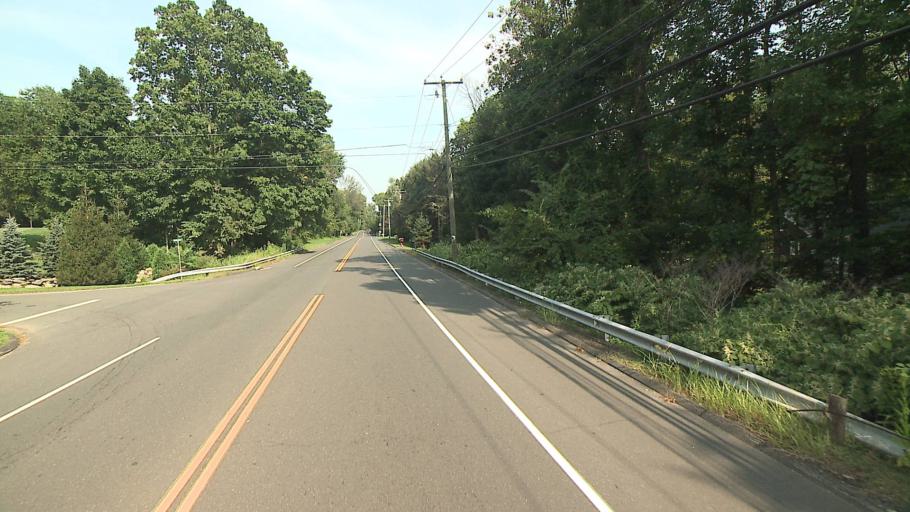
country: US
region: Connecticut
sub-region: Fairfield County
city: Westport
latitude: 41.1940
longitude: -73.3755
